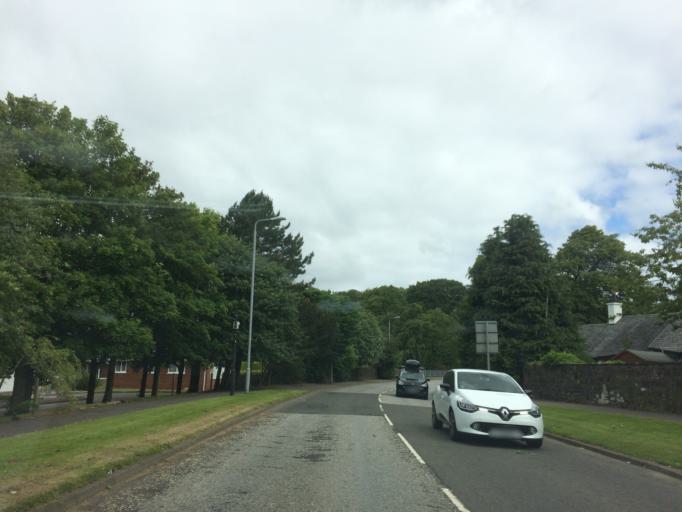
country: GB
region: Scotland
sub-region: East Renfrewshire
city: Newton Mearns
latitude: 55.7777
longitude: -4.3318
